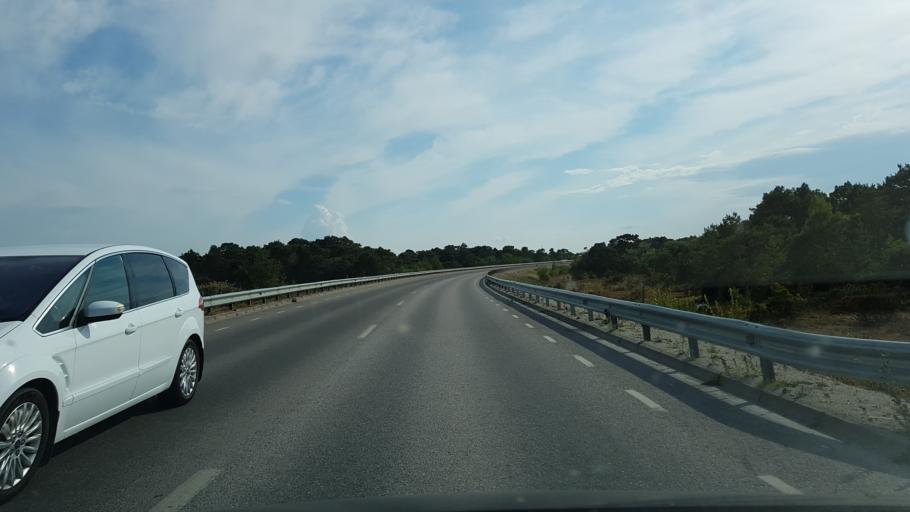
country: SE
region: Gotland
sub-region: Gotland
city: Visby
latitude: 57.6340
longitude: 18.3591
